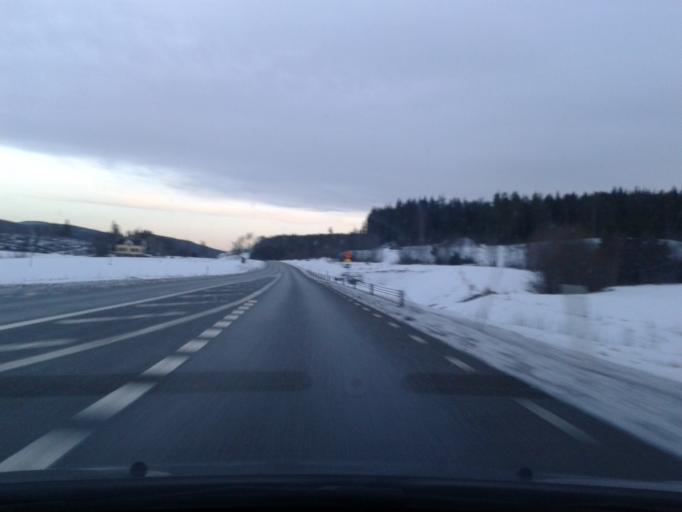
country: SE
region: Vaesternorrland
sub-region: Kramfors Kommun
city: Bollstabruk
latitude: 63.0391
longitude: 17.6490
